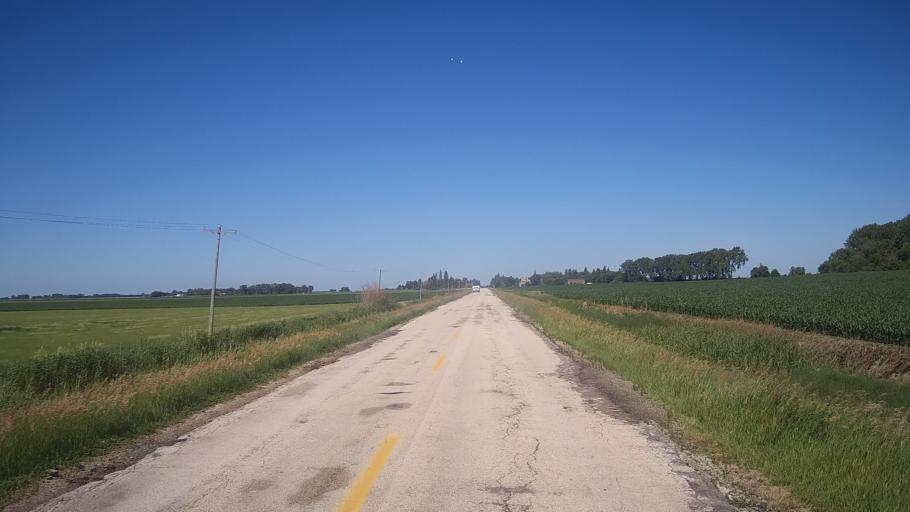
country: CA
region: Manitoba
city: Portage la Prairie
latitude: 50.0437
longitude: -98.0448
